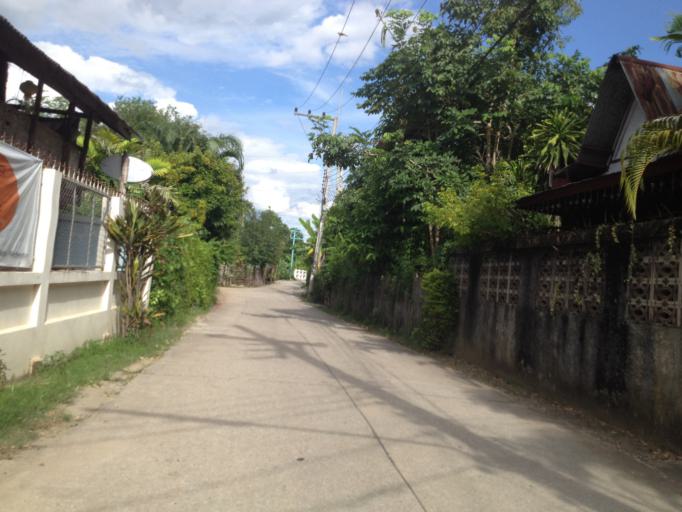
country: TH
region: Chiang Mai
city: Hang Dong
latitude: 18.7110
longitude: 98.9236
